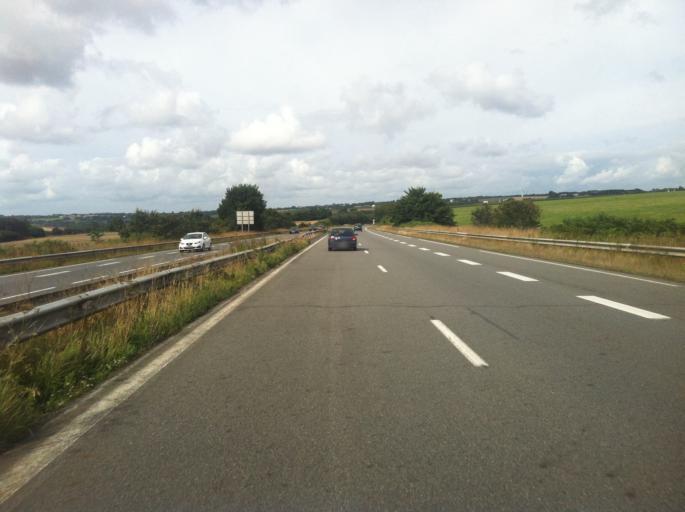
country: FR
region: Brittany
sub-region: Departement du Finistere
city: Saint-Thegonnec
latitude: 48.5280
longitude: -3.9432
